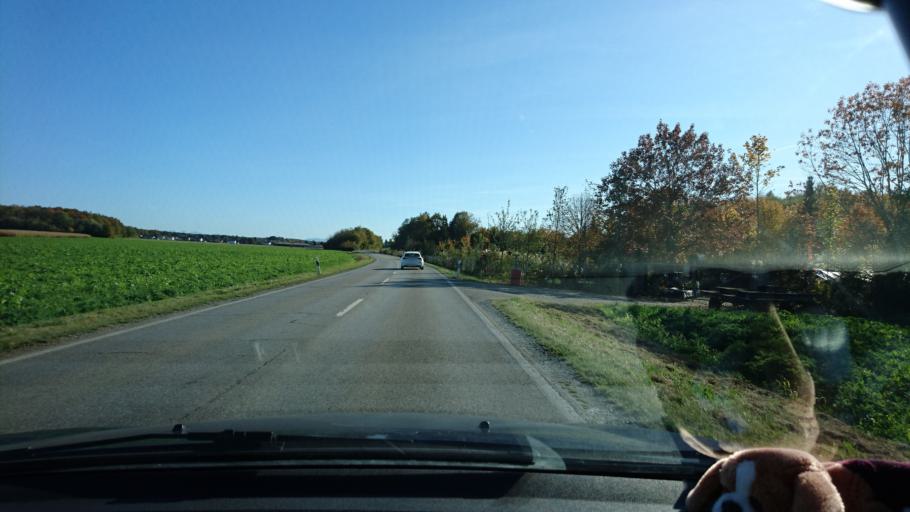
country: DE
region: Bavaria
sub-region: Upper Bavaria
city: Zorneding
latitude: 48.1073
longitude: 11.8298
